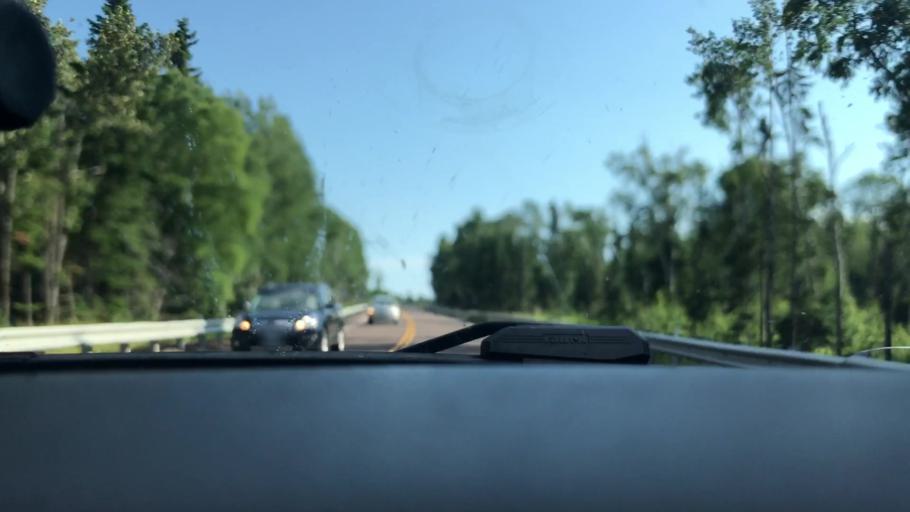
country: US
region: Minnesota
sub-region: Cook County
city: Grand Marais
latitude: 47.8374
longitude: -89.9730
